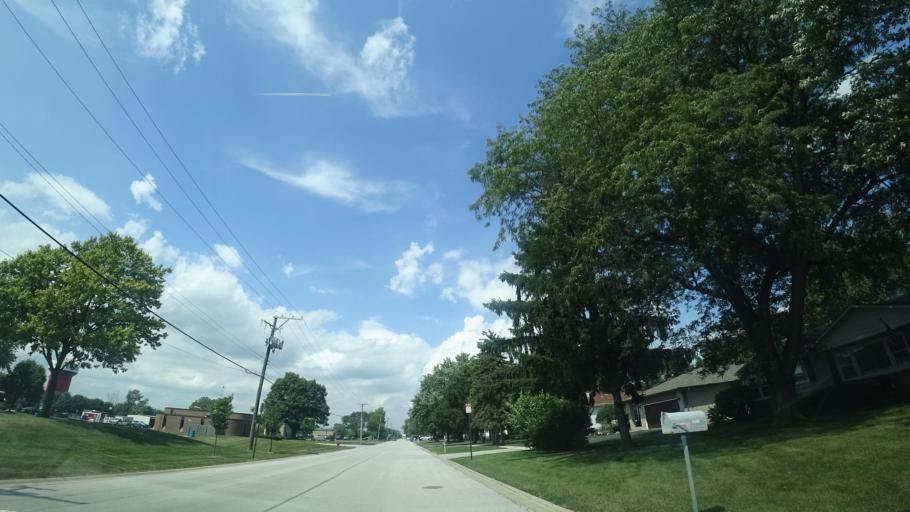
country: US
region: Illinois
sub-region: Cook County
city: Alsip
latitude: 41.6738
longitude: -87.7489
